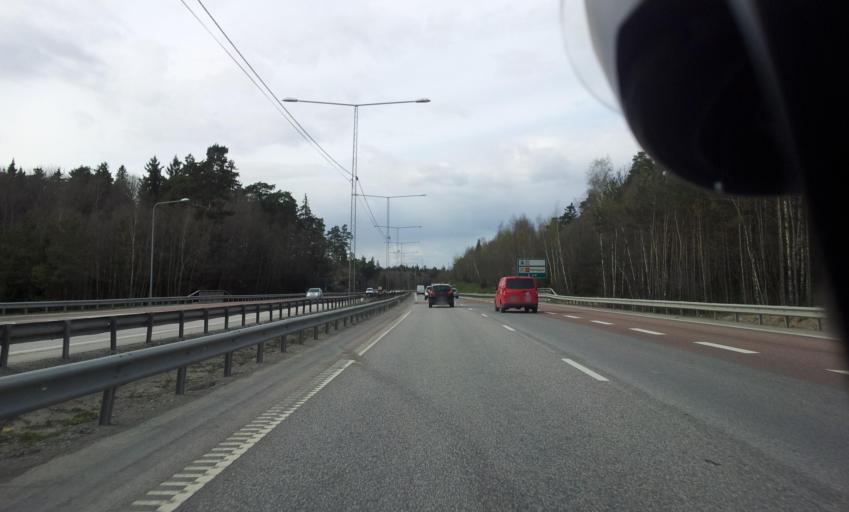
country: SE
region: Stockholm
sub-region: Jarfalla Kommun
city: Jakobsberg
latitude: 59.4512
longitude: 17.8365
